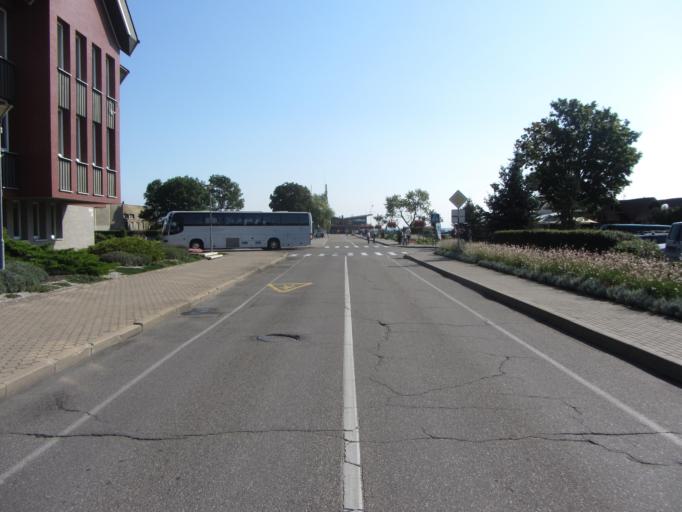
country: LT
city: Nida
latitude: 55.3031
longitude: 21.0059
